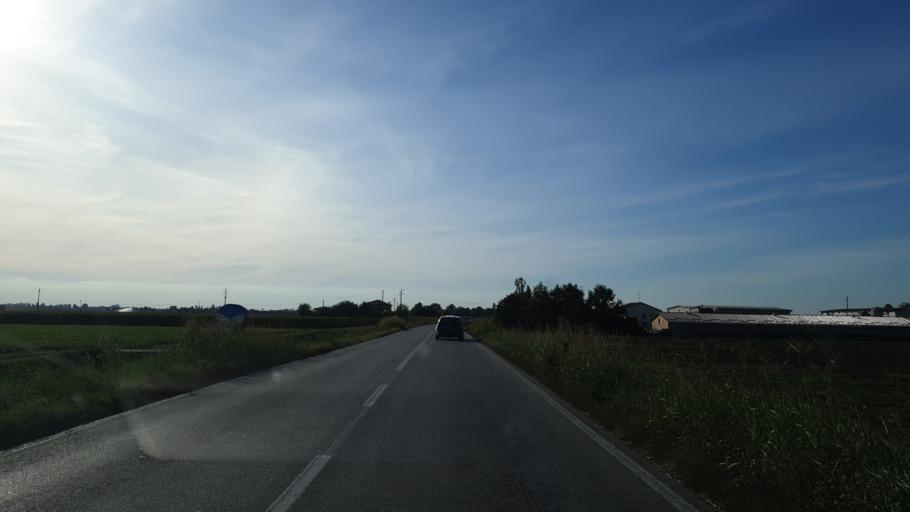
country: IT
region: Emilia-Romagna
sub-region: Provincia di Ravenna
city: Voltana
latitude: 44.5589
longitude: 11.9175
